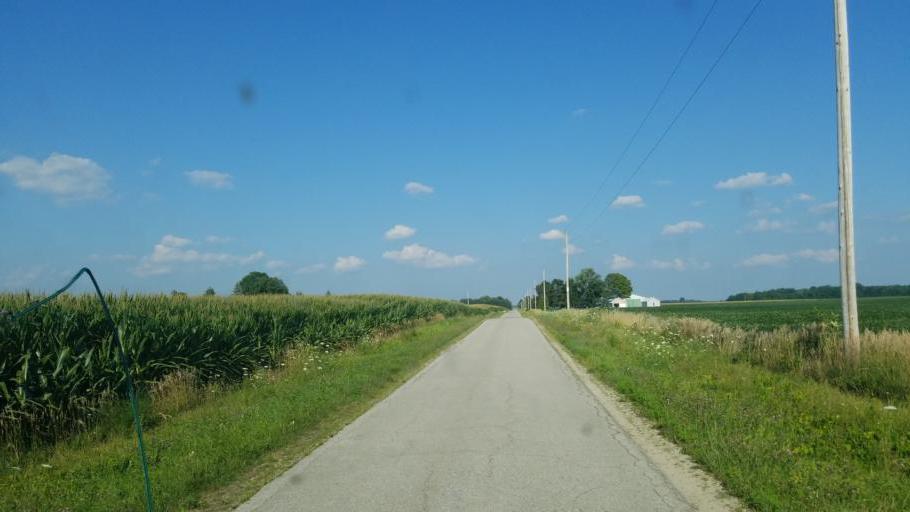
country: US
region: Ohio
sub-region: Crawford County
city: Bucyrus
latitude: 40.7897
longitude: -83.1041
